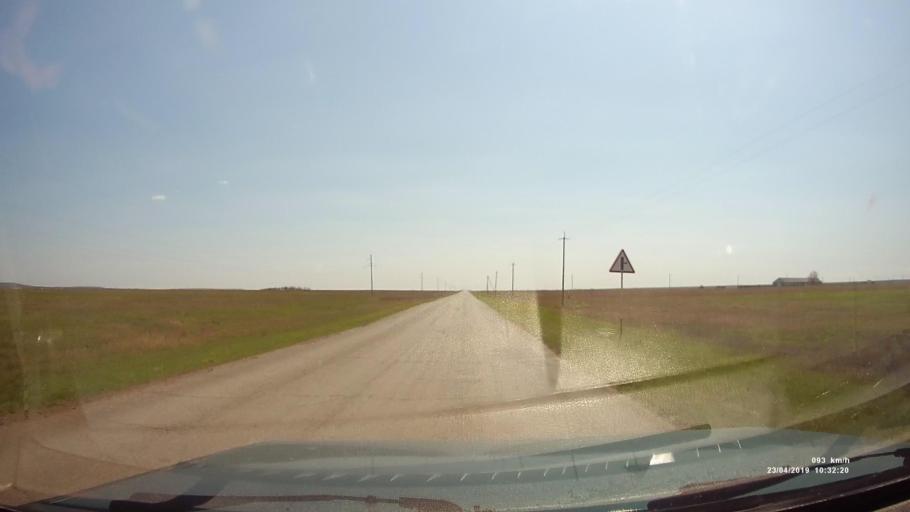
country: RU
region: Kalmykiya
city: Yashalta
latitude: 46.5809
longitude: 42.5762
